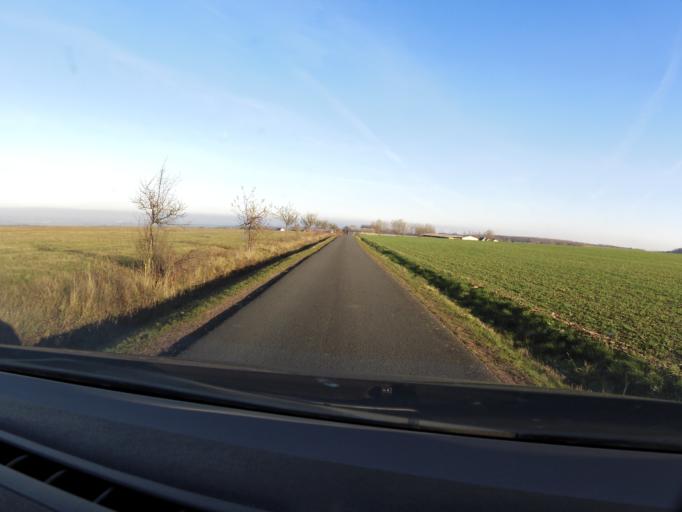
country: DE
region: Thuringia
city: Weberstedt
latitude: 51.0646
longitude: 10.4785
